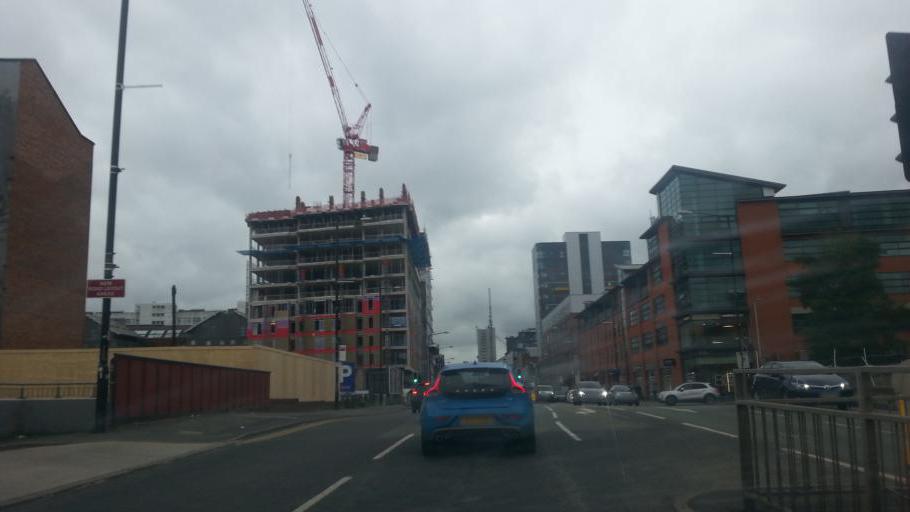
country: GB
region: England
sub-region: Manchester
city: Manchester
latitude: 53.4822
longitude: -2.2281
